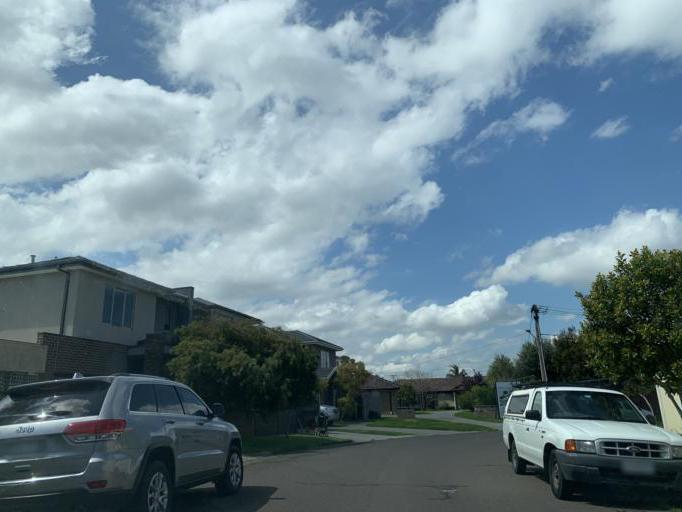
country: AU
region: Victoria
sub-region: Kingston
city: Mordialloc
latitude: -38.0013
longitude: 145.0897
